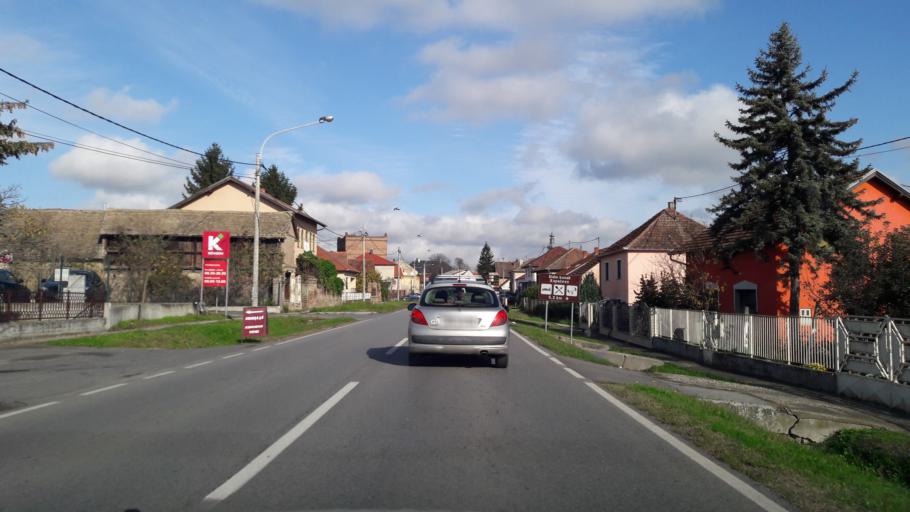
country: HR
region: Osjecko-Baranjska
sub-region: Grad Osijek
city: Bilje
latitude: 45.6006
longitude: 18.7434
